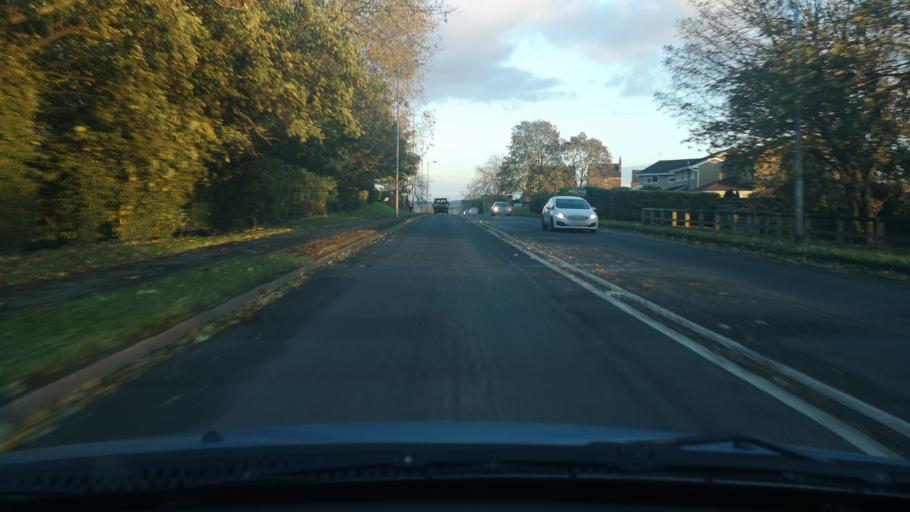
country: GB
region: England
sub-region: City and Borough of Wakefield
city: Horbury
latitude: 53.6577
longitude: -1.5606
